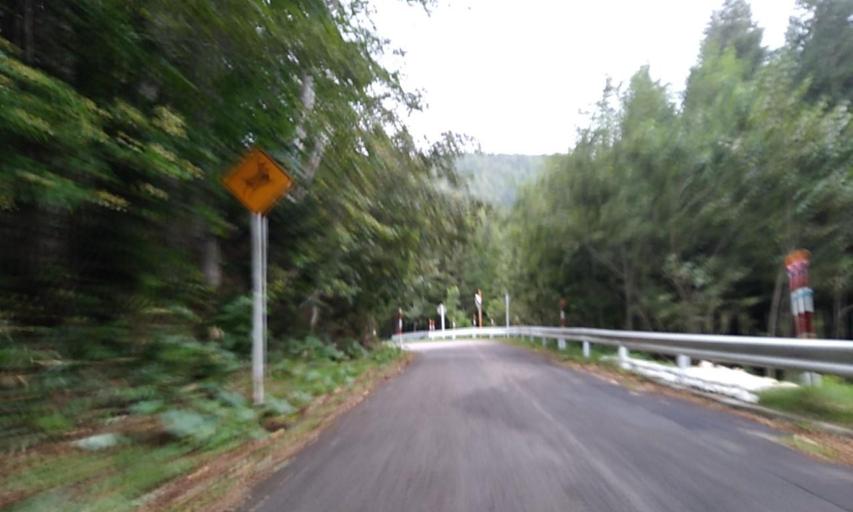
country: JP
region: Hokkaido
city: Bihoro
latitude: 43.5657
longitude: 144.1840
